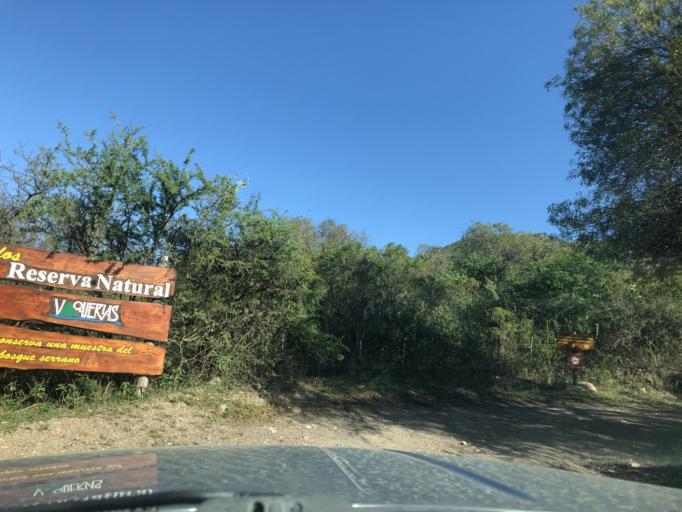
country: AR
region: Cordoba
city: Valle Hermoso
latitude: -31.1162
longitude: -64.4537
